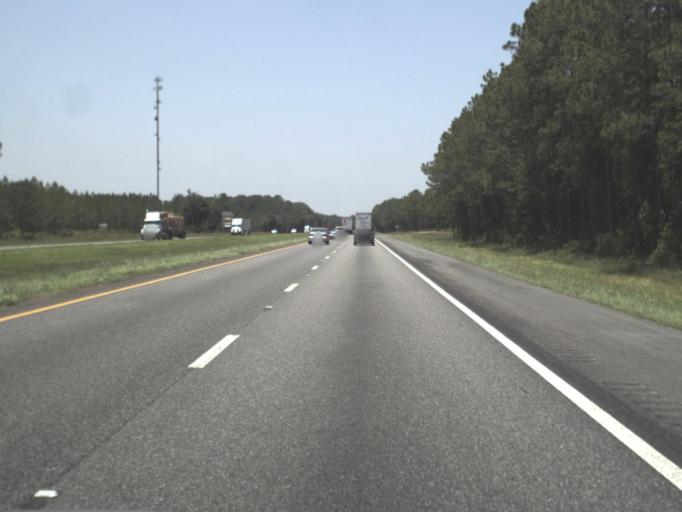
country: US
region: Florida
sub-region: Baker County
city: Macclenny
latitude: 30.2451
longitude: -82.3142
